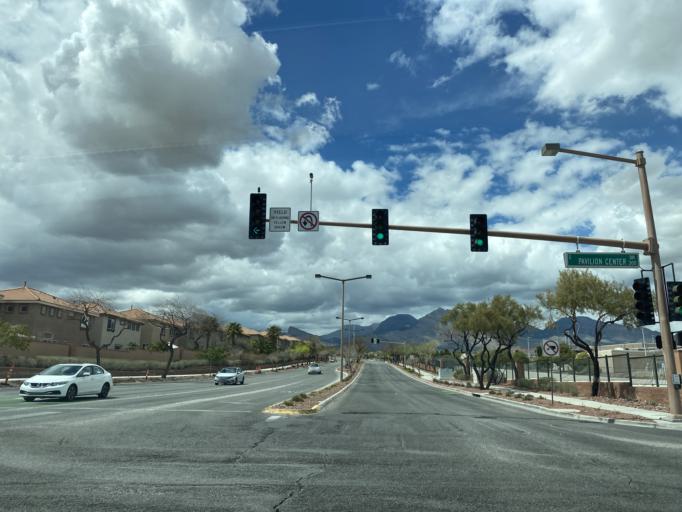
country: US
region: Nevada
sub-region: Clark County
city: Summerlin South
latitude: 36.1694
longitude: -115.3314
